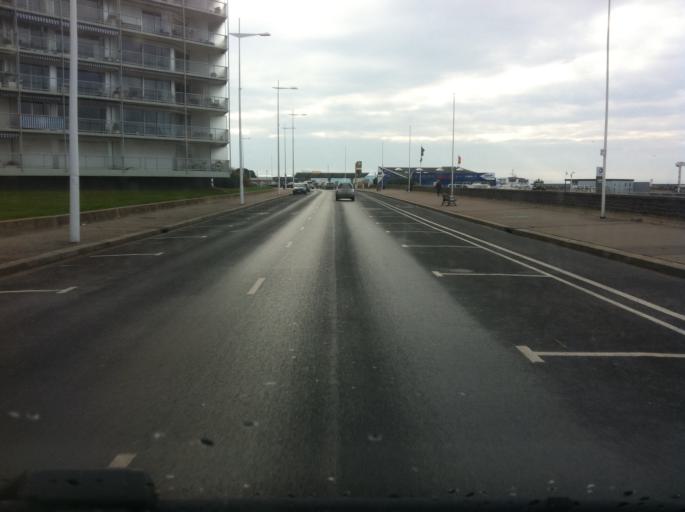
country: FR
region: Haute-Normandie
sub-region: Departement de la Seine-Maritime
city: Le Havre
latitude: 49.4881
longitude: 0.0983
